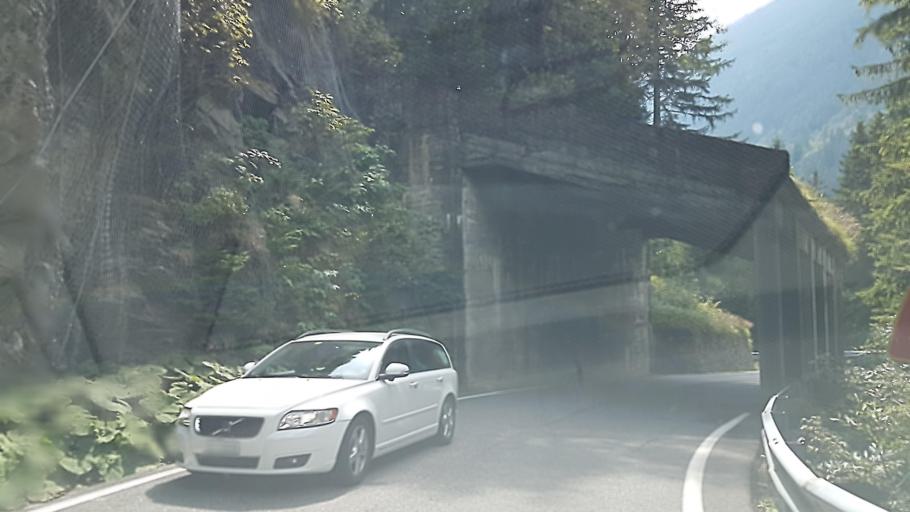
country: IT
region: Lombardy
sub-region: Provincia di Sondrio
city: Campodolcino
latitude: 46.4186
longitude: 9.3438
